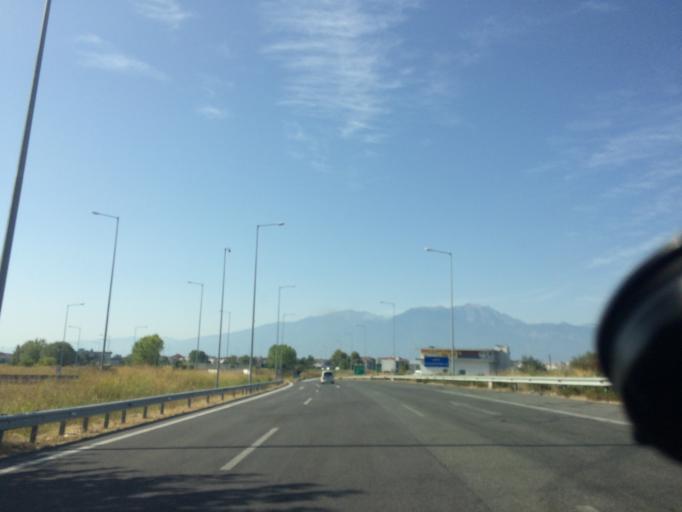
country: GR
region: Central Macedonia
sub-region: Nomos Pierias
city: Katerini
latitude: 40.2795
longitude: 22.5222
